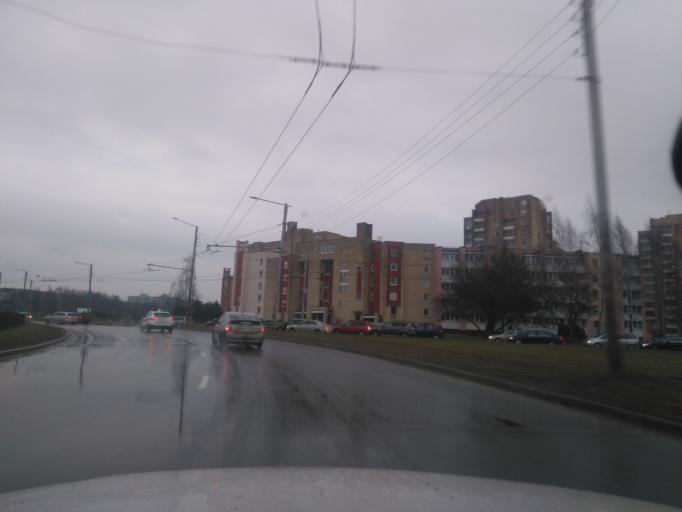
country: LT
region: Kauno apskritis
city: Dainava (Kaunas)
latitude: 54.9120
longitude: 23.9754
